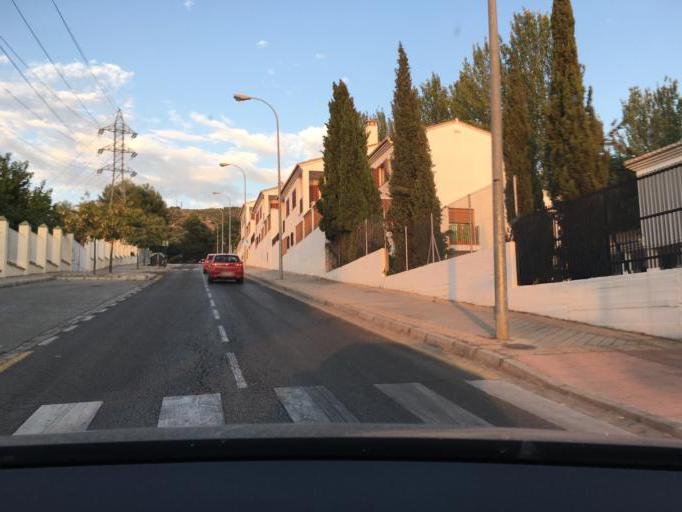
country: ES
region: Andalusia
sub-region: Provincia de Granada
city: Granada
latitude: 37.1893
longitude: -3.5949
